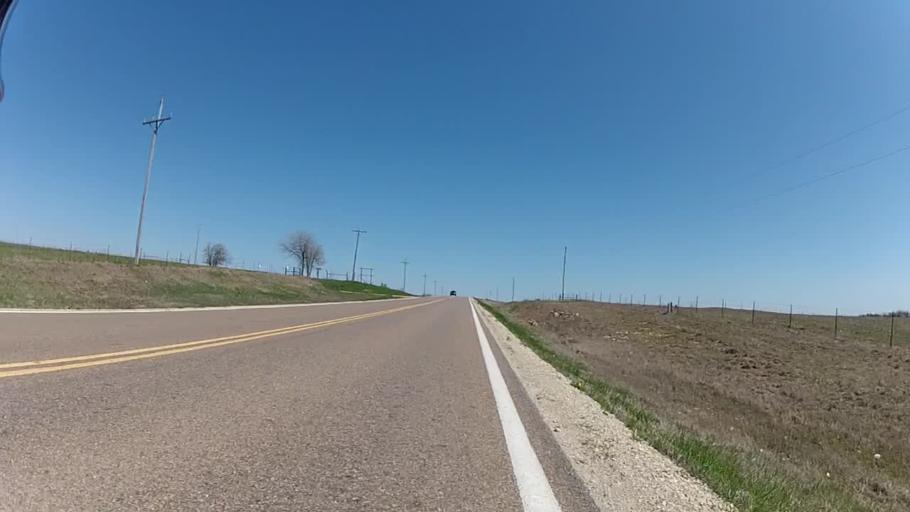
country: US
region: Kansas
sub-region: Morris County
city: Council Grove
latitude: 38.9126
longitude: -96.5202
